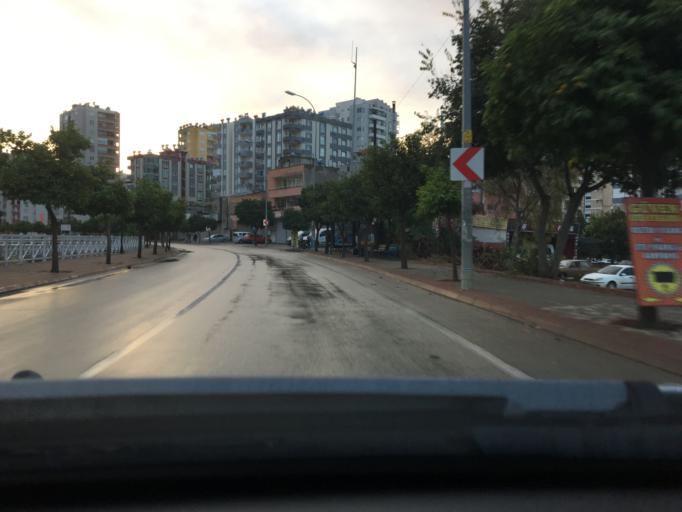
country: TR
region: Adana
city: Seyhan
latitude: 37.0285
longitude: 35.2831
